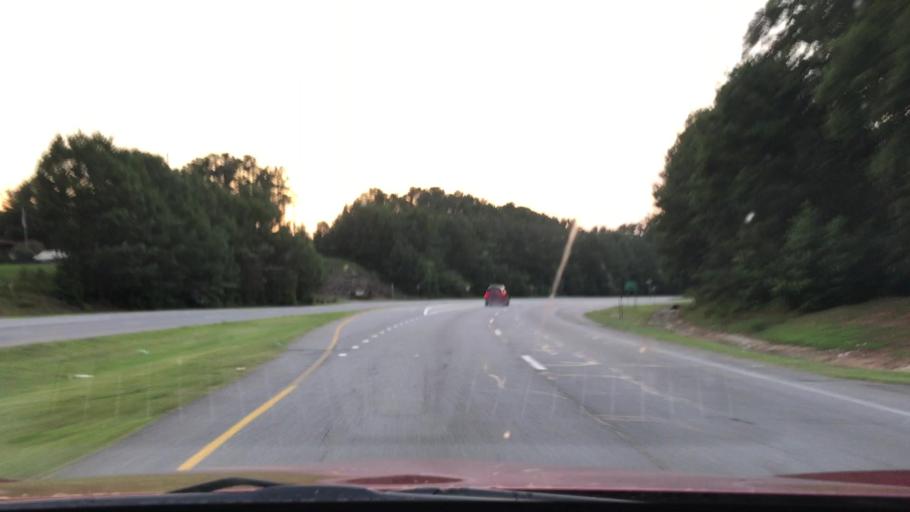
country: US
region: Georgia
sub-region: Gwinnett County
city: Lawrenceville
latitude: 33.9957
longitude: -83.9894
